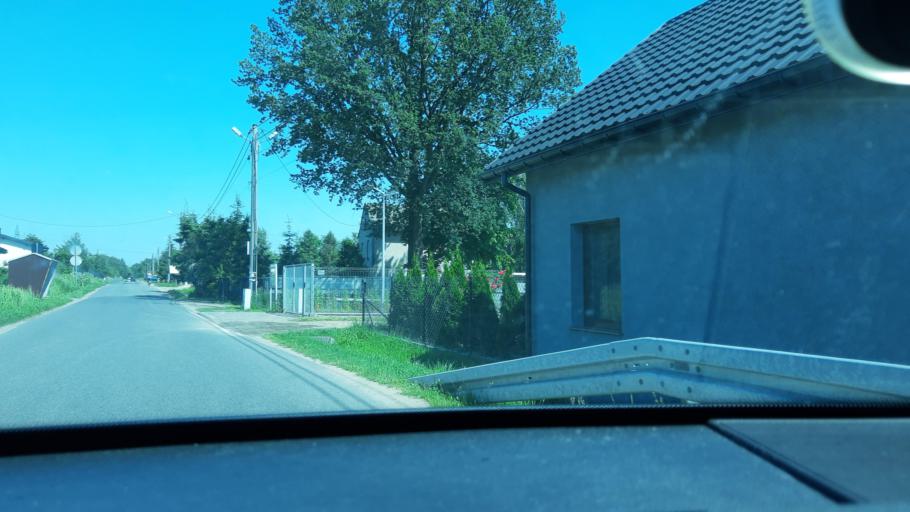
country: PL
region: Lodz Voivodeship
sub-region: Powiat zdunskowolski
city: Zdunska Wola
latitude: 51.6177
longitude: 18.9776
